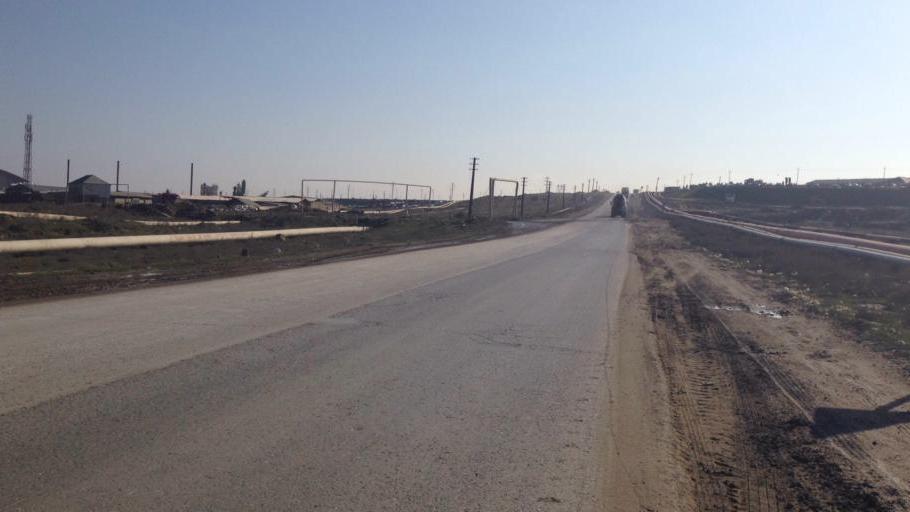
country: AZ
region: Abseron
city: Digah
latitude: 40.4670
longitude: 49.8867
